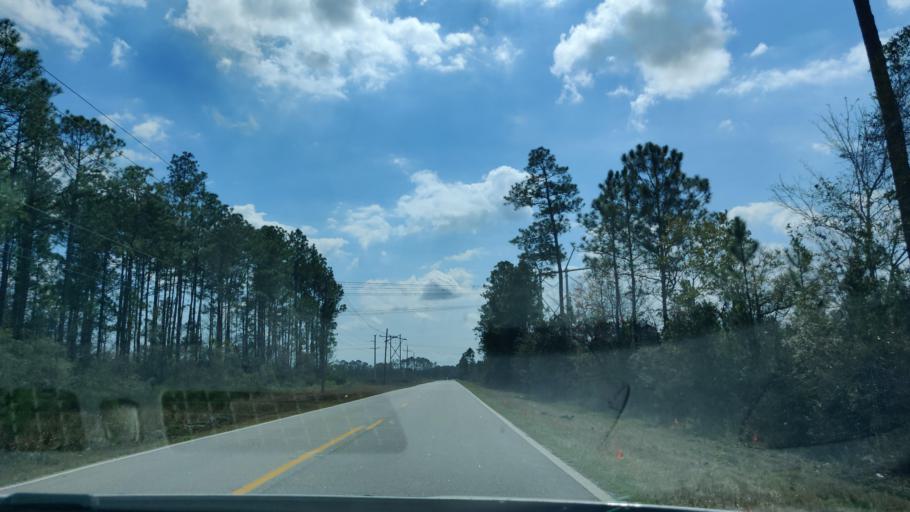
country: US
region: Florida
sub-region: Duval County
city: Baldwin
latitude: 30.2641
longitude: -81.9554
